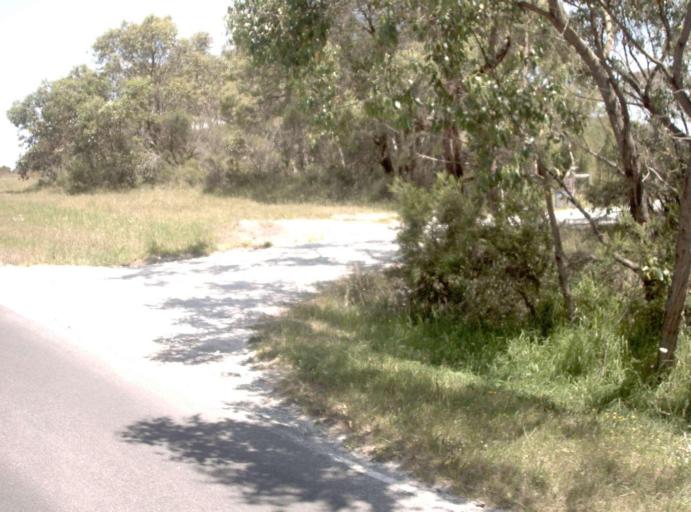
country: AU
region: Victoria
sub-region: Bass Coast
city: North Wonthaggi
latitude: -38.6655
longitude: 145.9269
